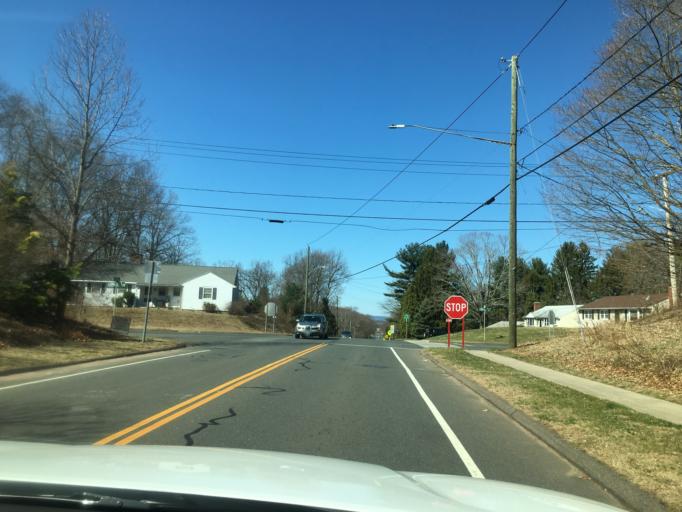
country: US
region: Connecticut
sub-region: Hartford County
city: East Hartford
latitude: 41.8059
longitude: -72.5932
